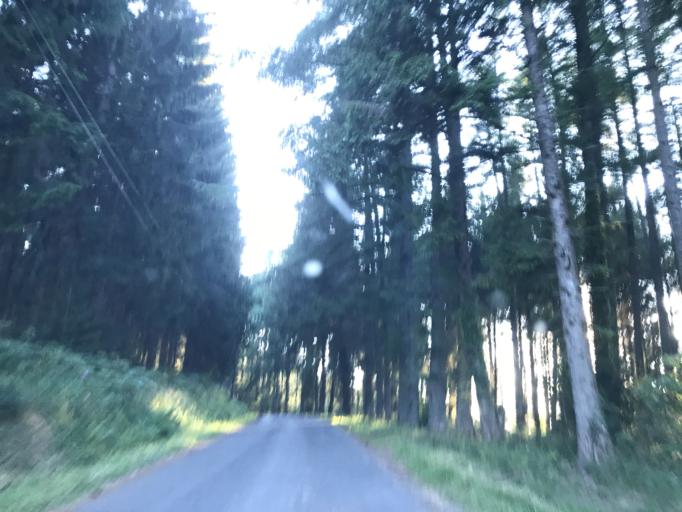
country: FR
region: Auvergne
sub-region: Departement du Puy-de-Dome
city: Celles-sur-Durolle
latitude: 45.7539
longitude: 3.6557
